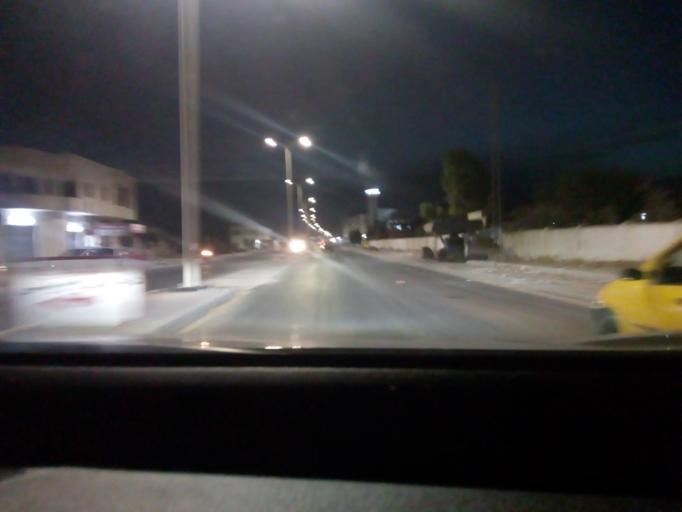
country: TN
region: Safaqis
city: Sfax
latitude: 34.7315
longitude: 10.6719
